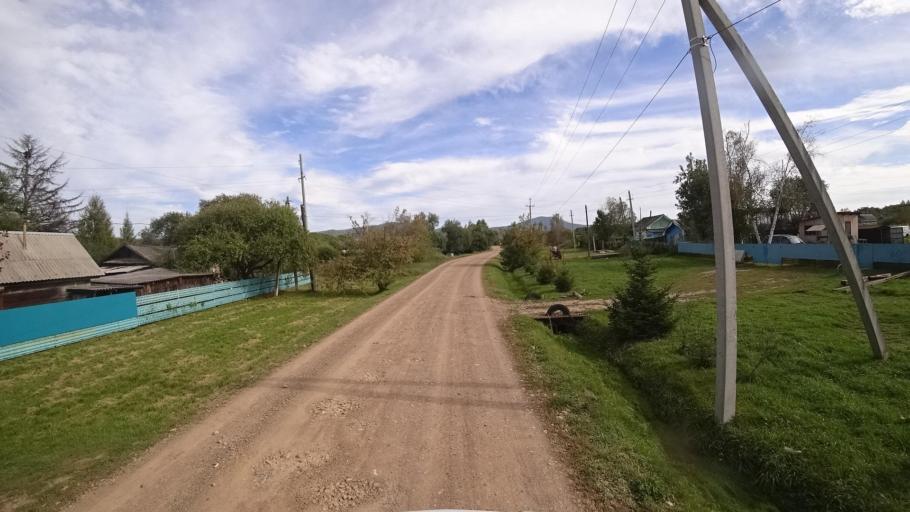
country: RU
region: Primorskiy
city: Dostoyevka
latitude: 44.3049
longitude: 133.4603
